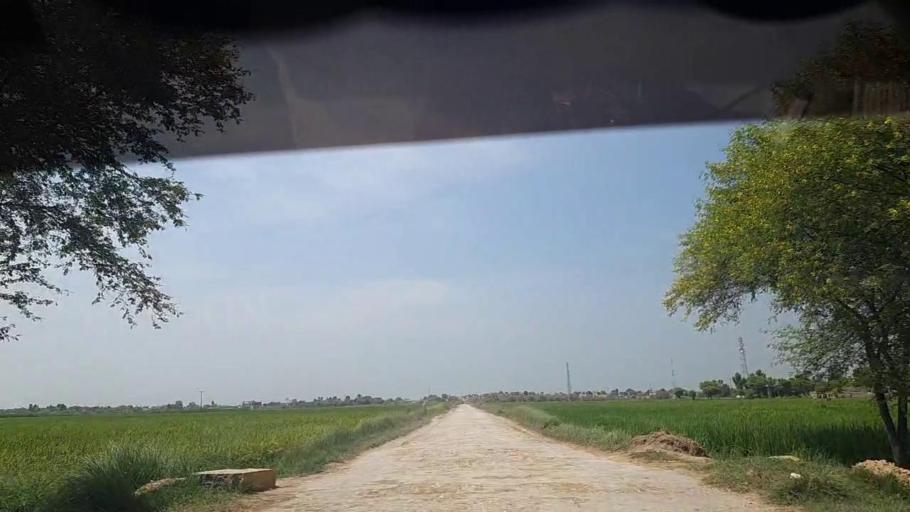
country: PK
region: Sindh
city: Thul
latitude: 28.1761
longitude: 68.7368
